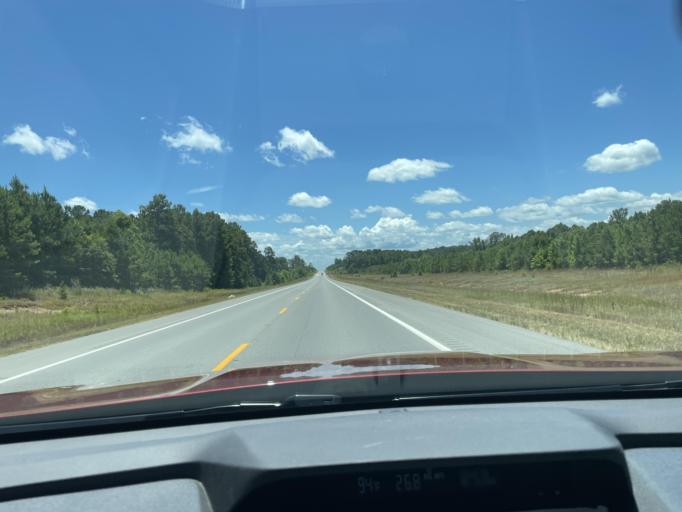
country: US
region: Arkansas
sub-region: Lincoln County
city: Star City
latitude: 33.9057
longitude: -91.8832
